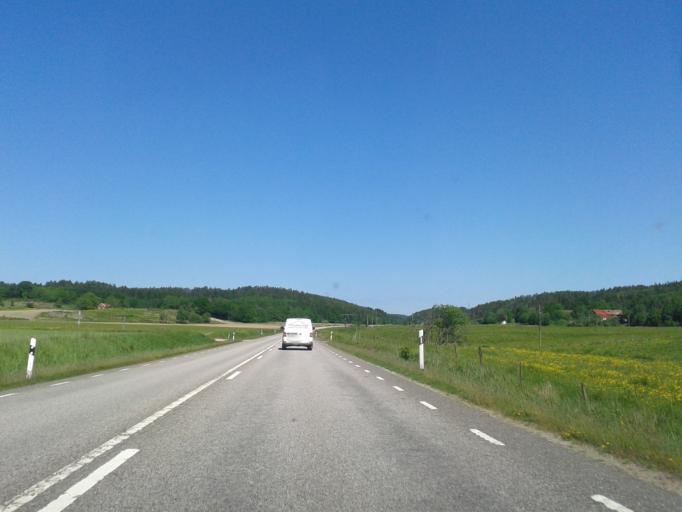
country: SE
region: Vaestra Goetaland
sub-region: Orust
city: Henan
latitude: 58.1677
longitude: 11.7028
